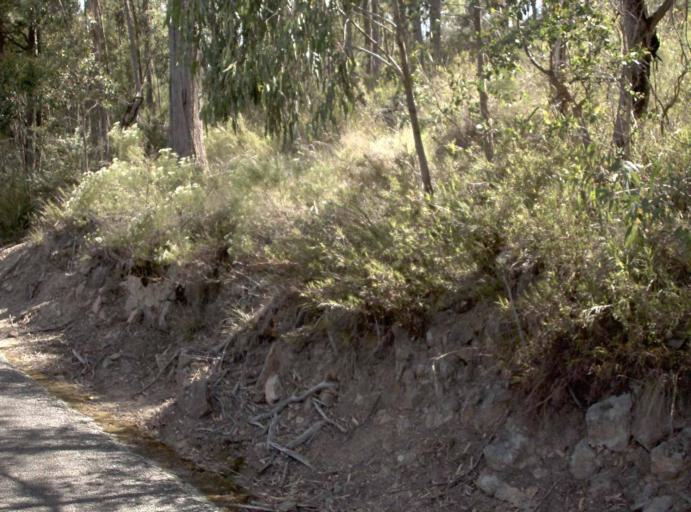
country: AU
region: Victoria
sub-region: East Gippsland
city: Lakes Entrance
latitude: -37.4862
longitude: 148.1278
